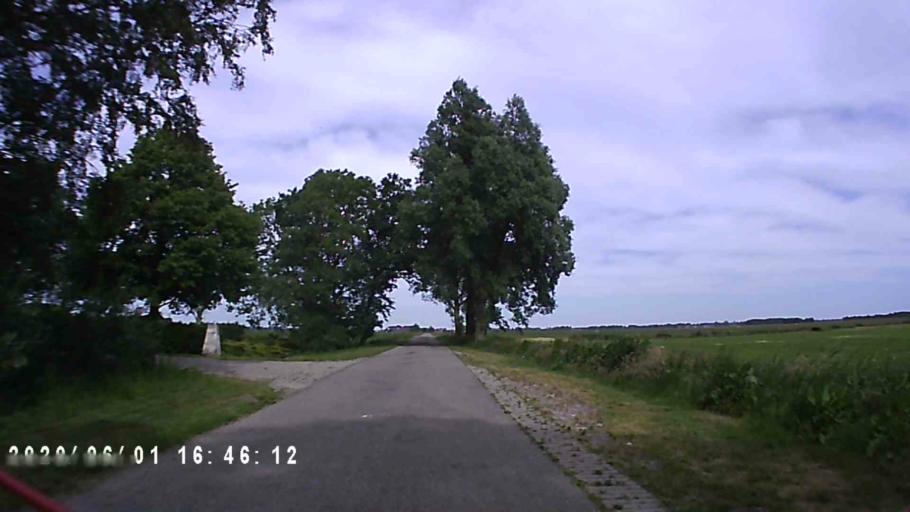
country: NL
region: Friesland
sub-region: Gemeente Tytsjerksteradiel
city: Tytsjerk
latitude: 53.1859
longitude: 5.8906
